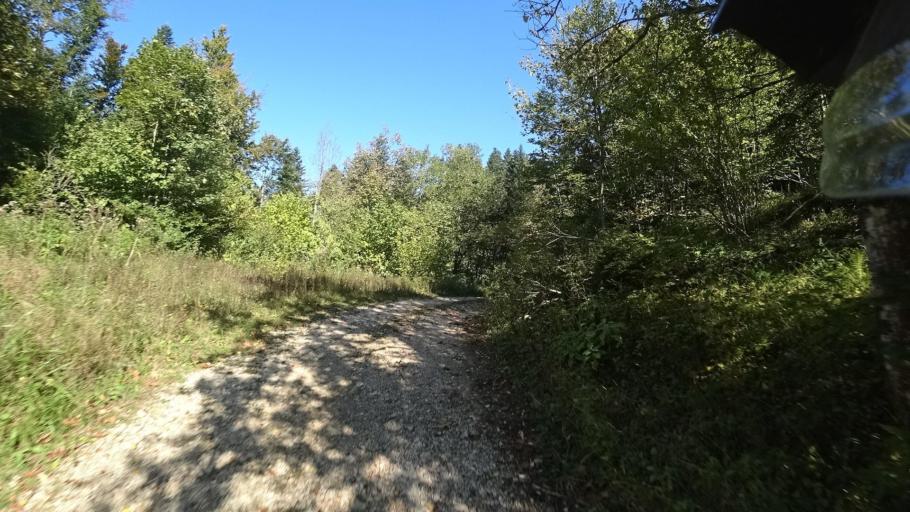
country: HR
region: Karlovacka
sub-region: Grad Ogulin
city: Ogulin
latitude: 45.1716
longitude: 15.1614
